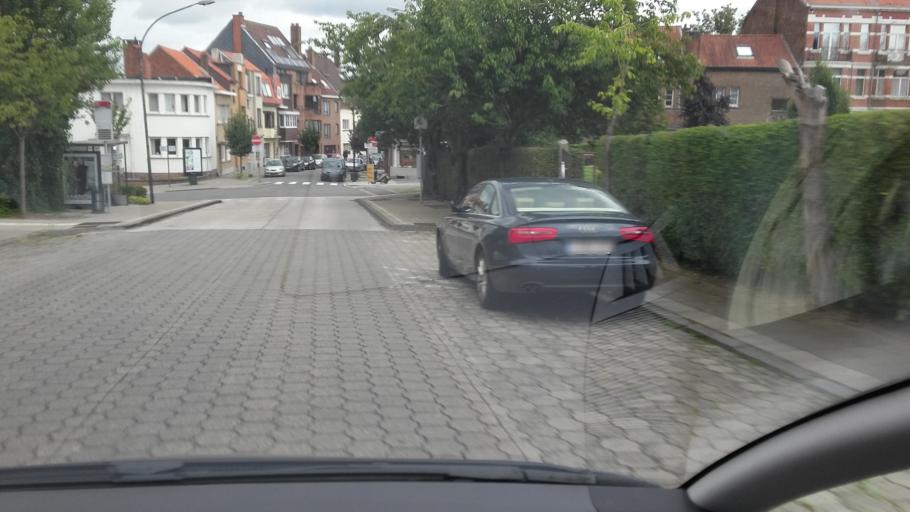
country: BE
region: Flanders
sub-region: Provincie Vlaams-Brabant
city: Hoeilaart
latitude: 50.8108
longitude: 4.4184
